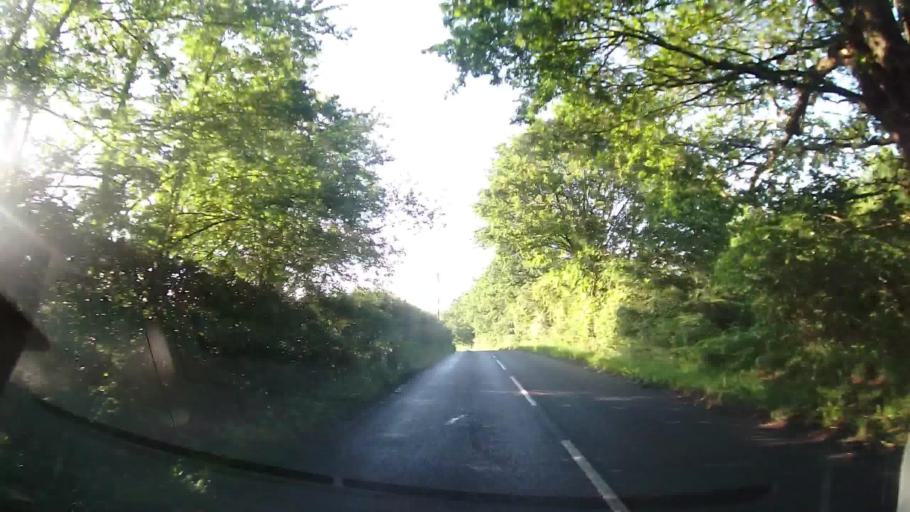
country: GB
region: England
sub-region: Leicestershire
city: Markfield
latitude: 52.6603
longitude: -1.2655
